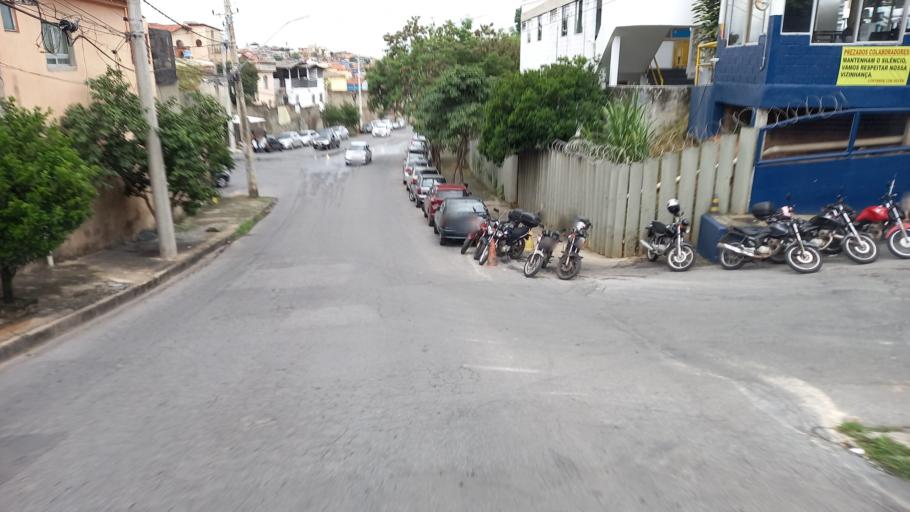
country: BR
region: Minas Gerais
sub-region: Belo Horizonte
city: Belo Horizonte
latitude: -19.8868
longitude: -43.8936
